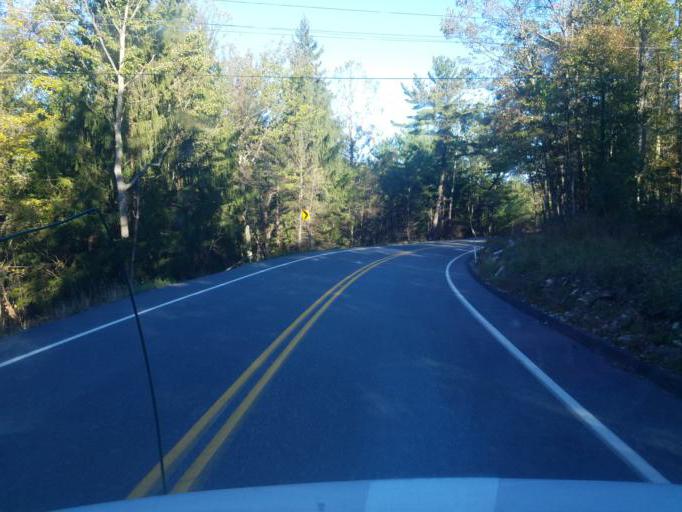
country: US
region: Pennsylvania
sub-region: Franklin County
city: Mont Alto
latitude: 39.8460
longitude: -77.5168
